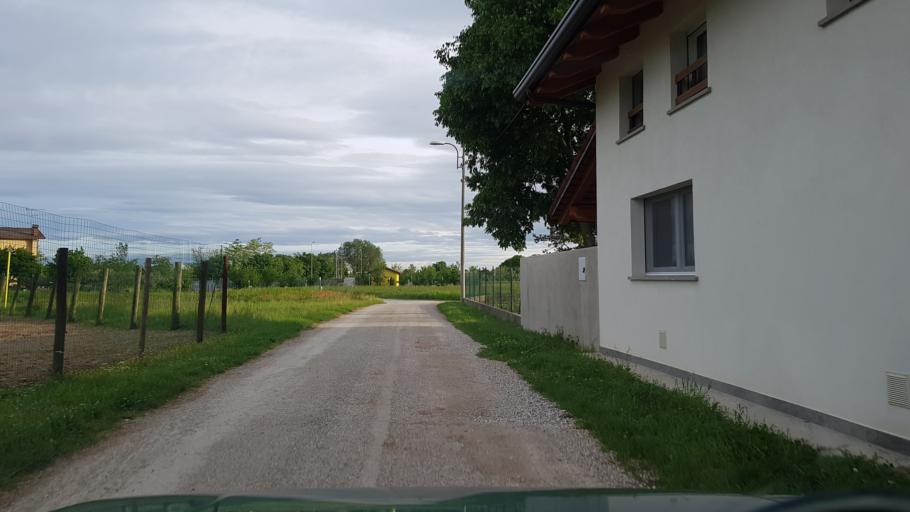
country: IT
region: Friuli Venezia Giulia
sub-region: Provincia di Gorizia
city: Sagrado
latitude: 45.8891
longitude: 13.4665
